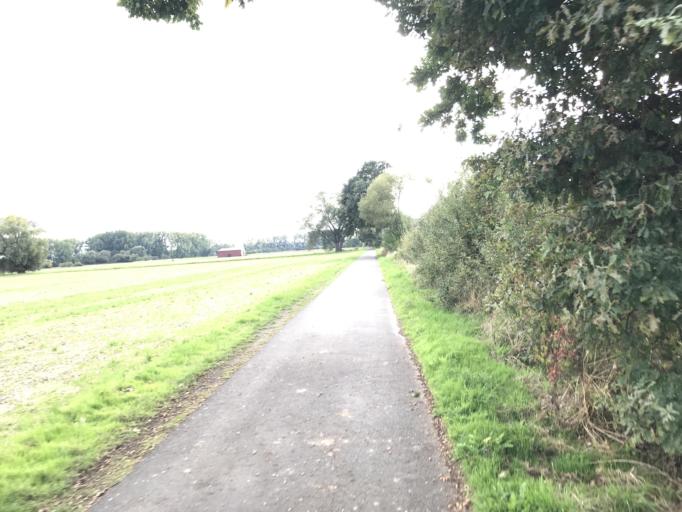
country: DE
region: Hesse
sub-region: Regierungsbezirk Kassel
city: Wabern
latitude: 51.0812
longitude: 9.3408
